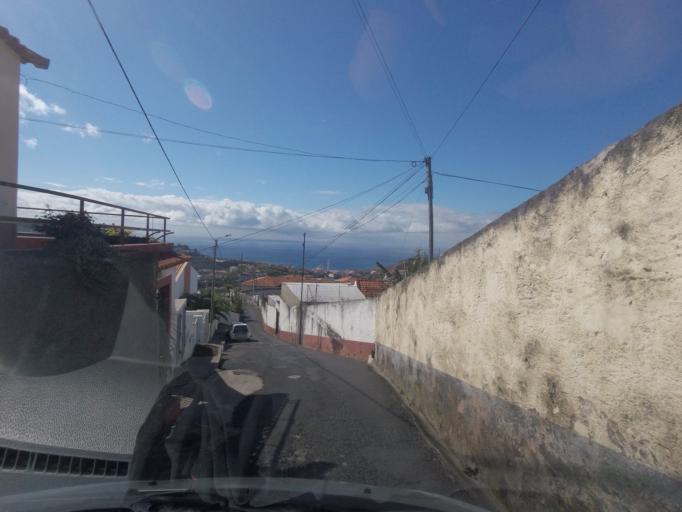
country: PT
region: Madeira
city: Camara de Lobos
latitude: 32.6616
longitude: -16.9738
